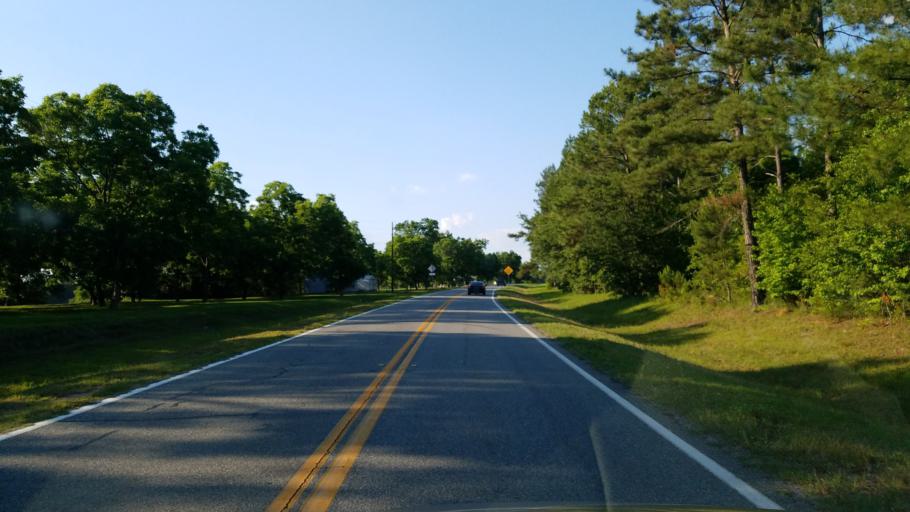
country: US
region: Georgia
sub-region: Lanier County
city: Lakeland
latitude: 30.9707
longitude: -83.0820
